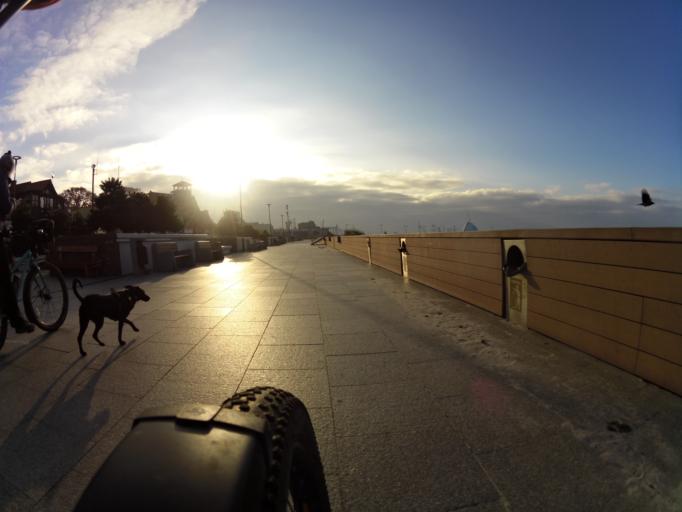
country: PL
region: Pomeranian Voivodeship
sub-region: Powiat pucki
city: Hel
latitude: 54.6060
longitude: 18.8007
